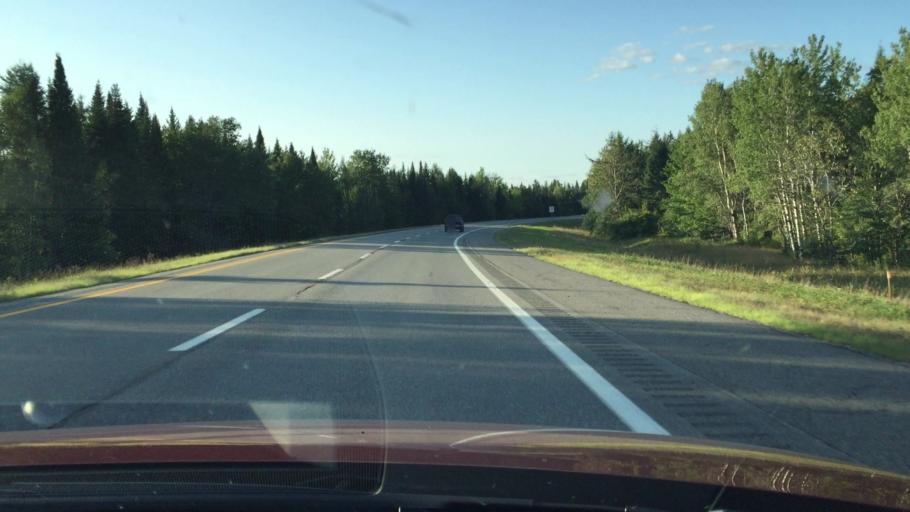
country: US
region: Maine
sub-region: Penobscot County
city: Patten
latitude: 46.0172
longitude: -68.2882
